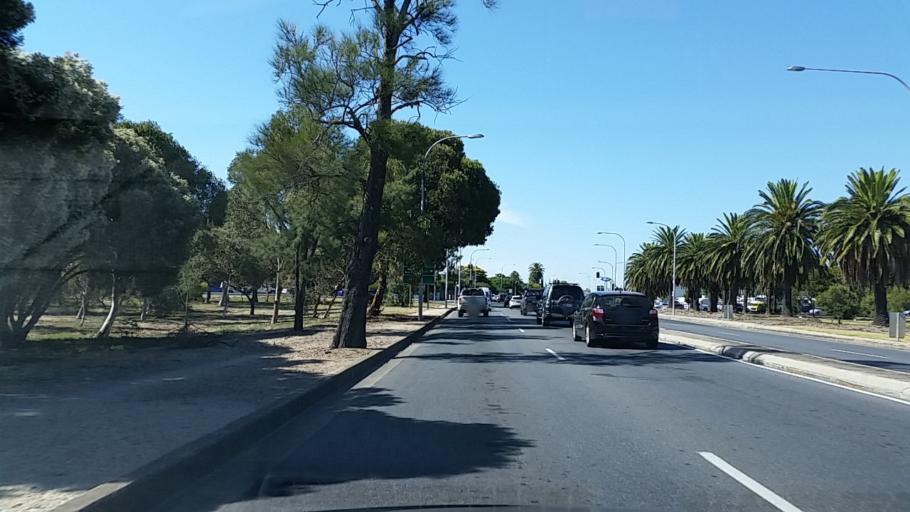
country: AU
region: South Australia
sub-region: Adelaide
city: North Adelaide
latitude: -34.8997
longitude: 138.5963
